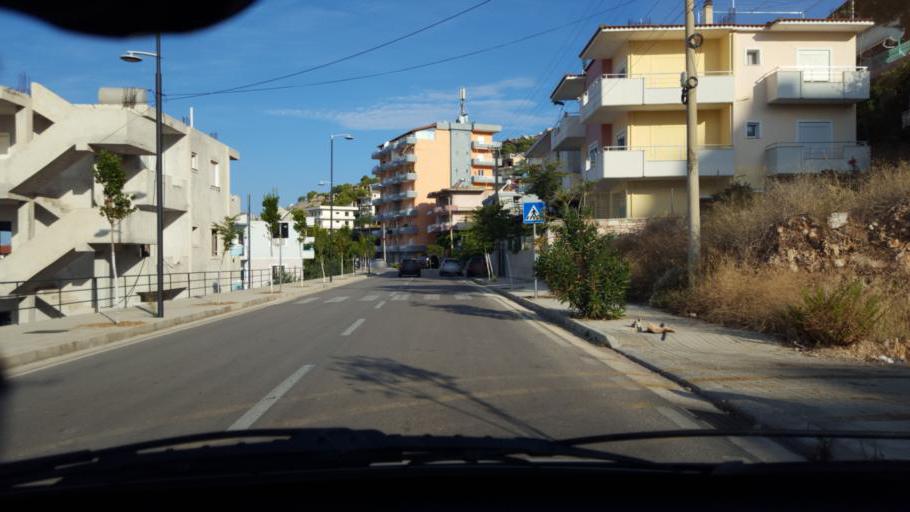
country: AL
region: Vlore
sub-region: Rrethi i Sarandes
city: Sarande
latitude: 39.8757
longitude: 19.9972
